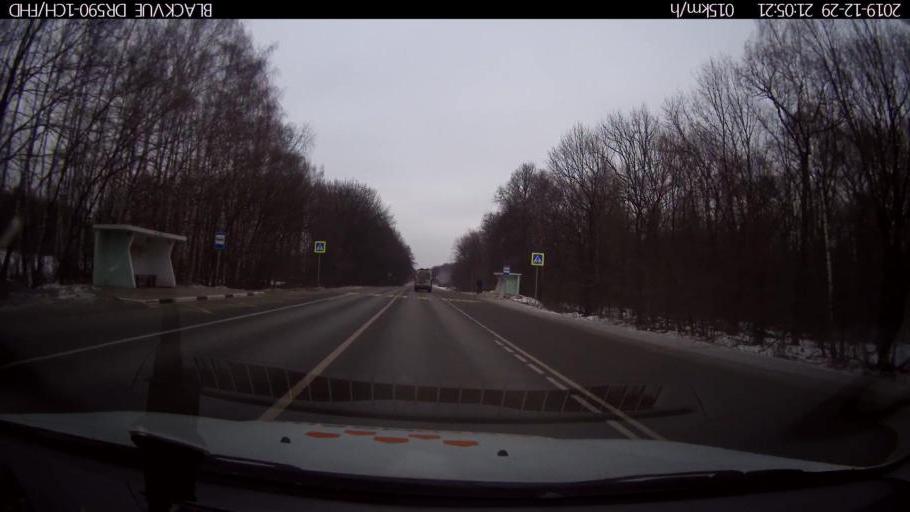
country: RU
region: Nizjnij Novgorod
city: Afonino
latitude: 56.2087
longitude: 43.9988
